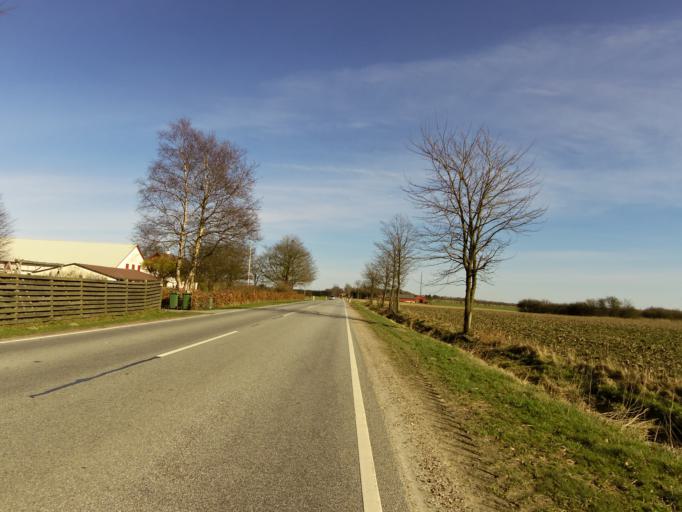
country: DK
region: South Denmark
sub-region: Vejen Kommune
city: Rodding
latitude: 55.3616
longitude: 9.1137
